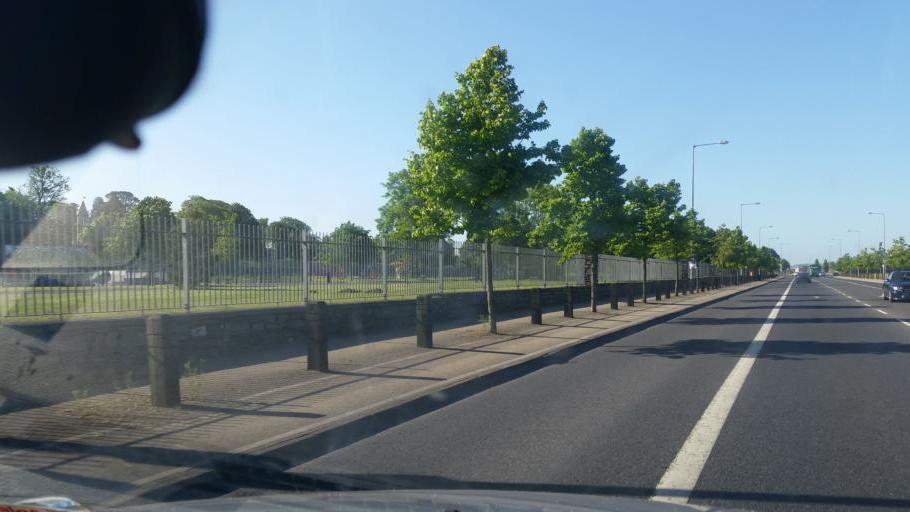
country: IE
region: Leinster
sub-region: Fingal County
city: Blanchardstown
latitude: 53.3891
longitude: -6.4009
